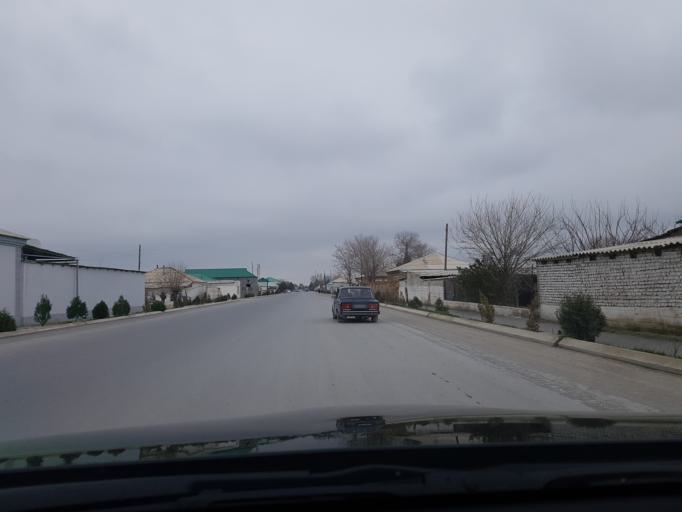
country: TM
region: Ahal
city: Abadan
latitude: 38.1497
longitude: 57.9568
